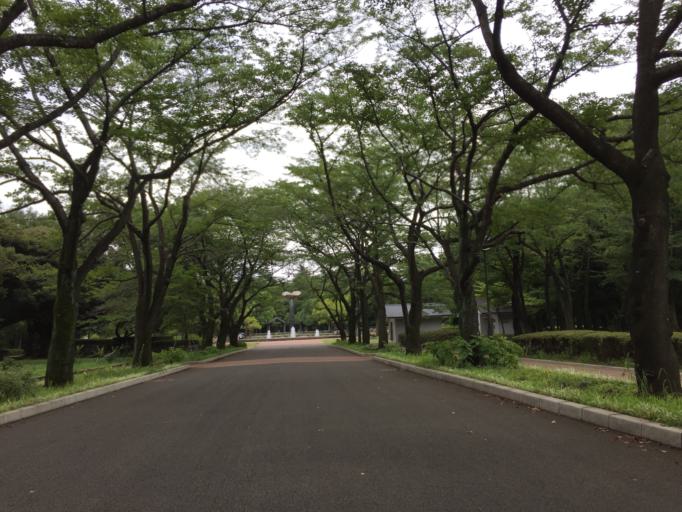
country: JP
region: Tokyo
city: Kokubunji
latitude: 35.6764
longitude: 139.4918
